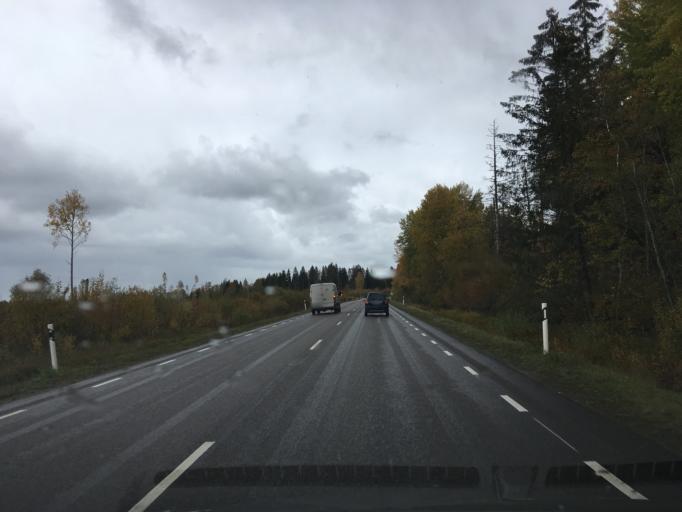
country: EE
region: Harju
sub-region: Anija vald
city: Kehra
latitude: 59.3373
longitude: 25.3109
